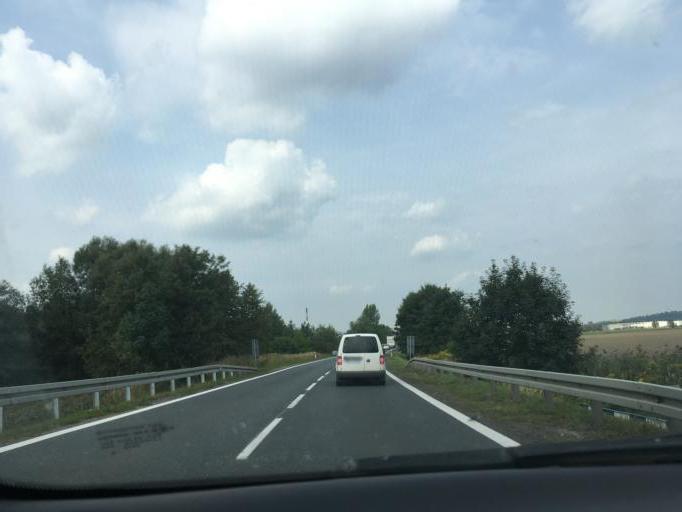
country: PL
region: Silesian Voivodeship
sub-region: Powiat bierunsko-ledzinski
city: Bierun
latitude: 50.0867
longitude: 19.1097
